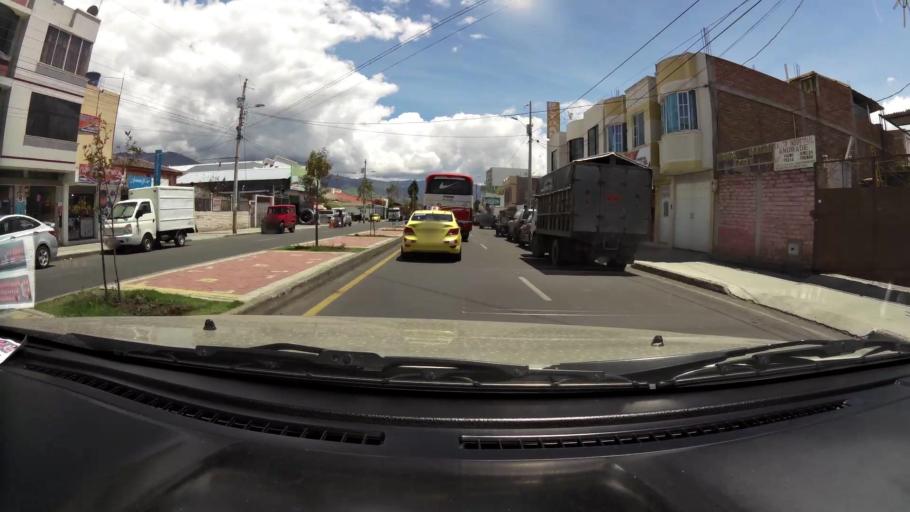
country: EC
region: Chimborazo
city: Riobamba
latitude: -1.6853
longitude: -78.6350
